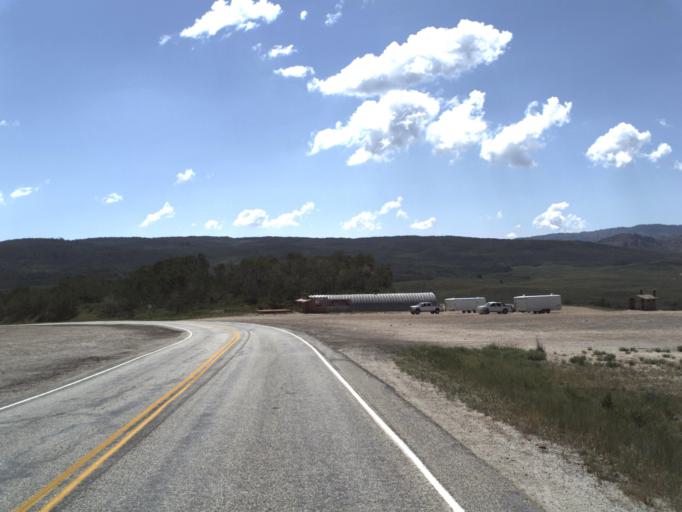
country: US
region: Utah
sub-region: Weber County
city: Wolf Creek
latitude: 41.4124
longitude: -111.5799
